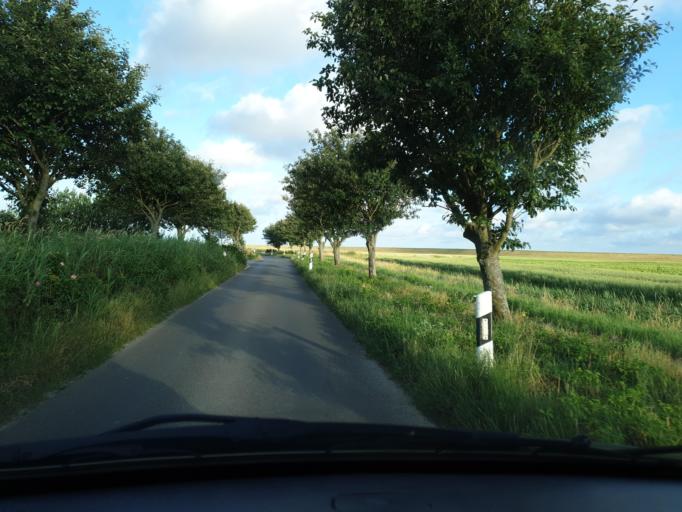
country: DE
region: Schleswig-Holstein
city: Busumer Deichhausen
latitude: 54.1397
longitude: 8.9060
